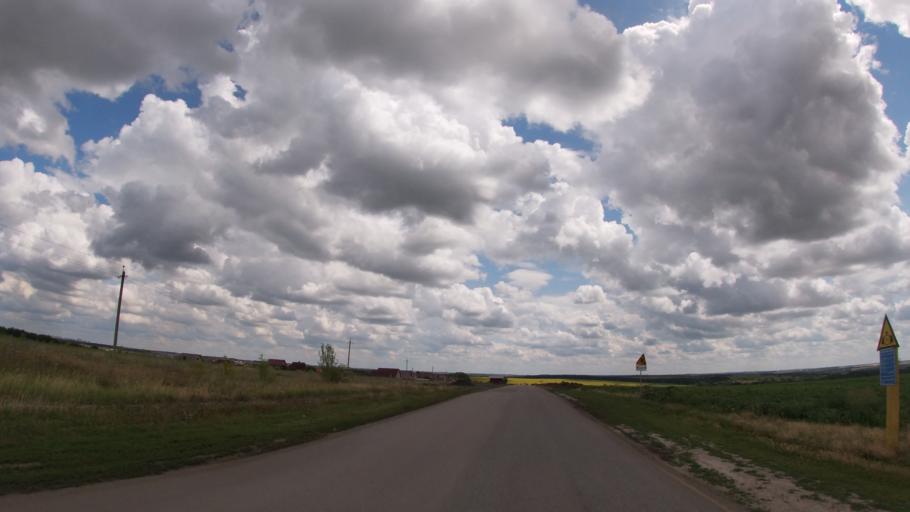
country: RU
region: Belgorod
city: Mayskiy
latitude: 50.5026
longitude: 36.4426
